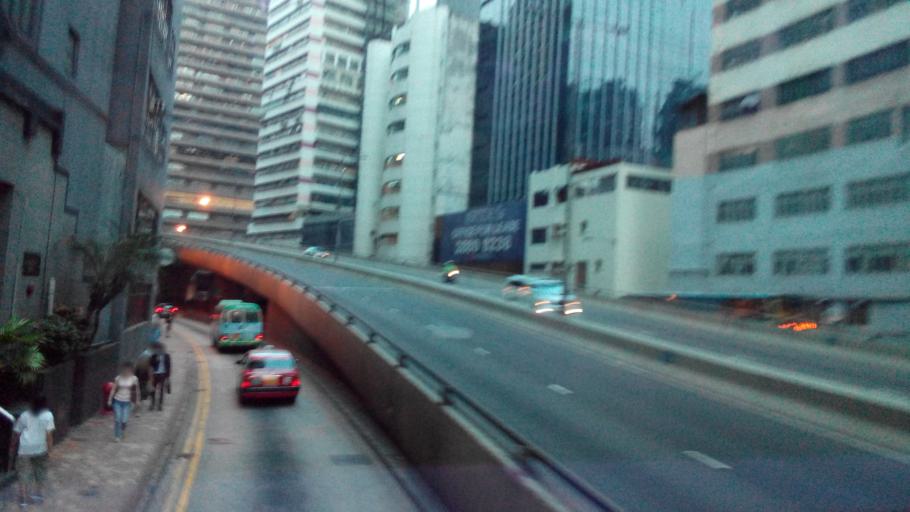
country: HK
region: Wanchai
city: Wan Chai
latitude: 22.2484
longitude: 114.1646
